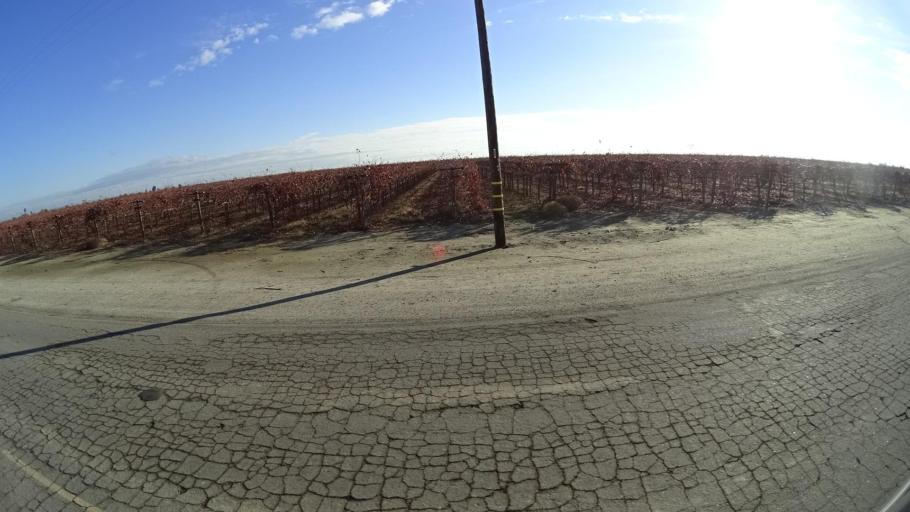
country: US
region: California
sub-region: Kern County
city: Delano
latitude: 35.7633
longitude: -119.2852
